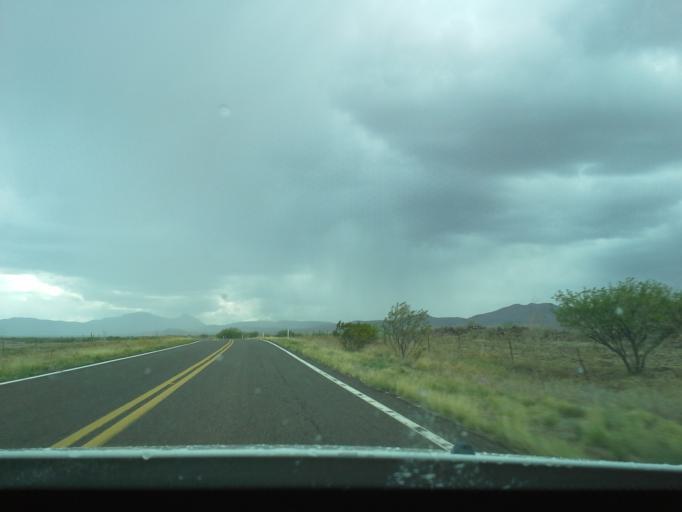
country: US
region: Arizona
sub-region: Cochise County
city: Douglas
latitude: 31.5478
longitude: -109.2794
